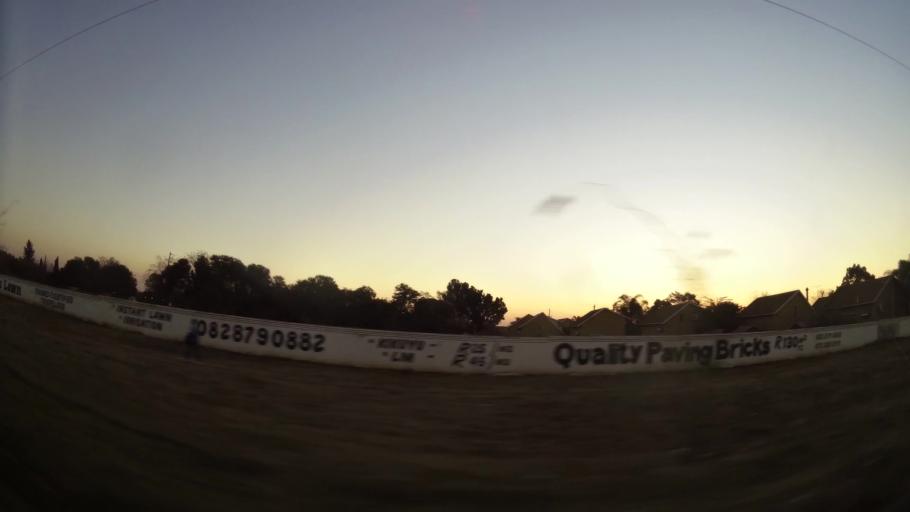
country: ZA
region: Gauteng
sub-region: City of Tshwane Metropolitan Municipality
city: Centurion
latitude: -25.8634
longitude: 28.1371
